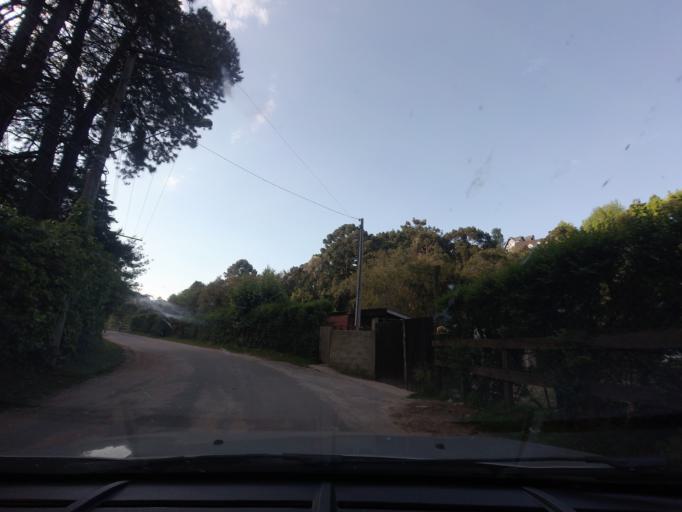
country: BR
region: Sao Paulo
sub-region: Campos Do Jordao
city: Campos do Jordao
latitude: -22.7187
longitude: -45.5579
